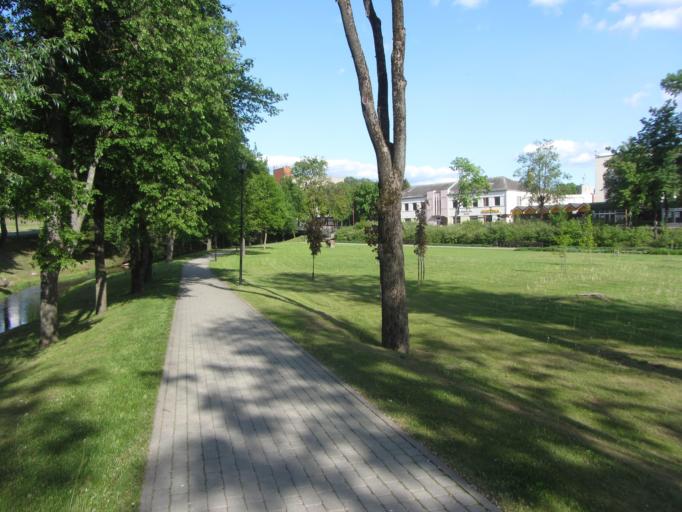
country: LT
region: Utenos apskritis
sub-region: Utena
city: Utena
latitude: 55.4985
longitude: 25.5983
